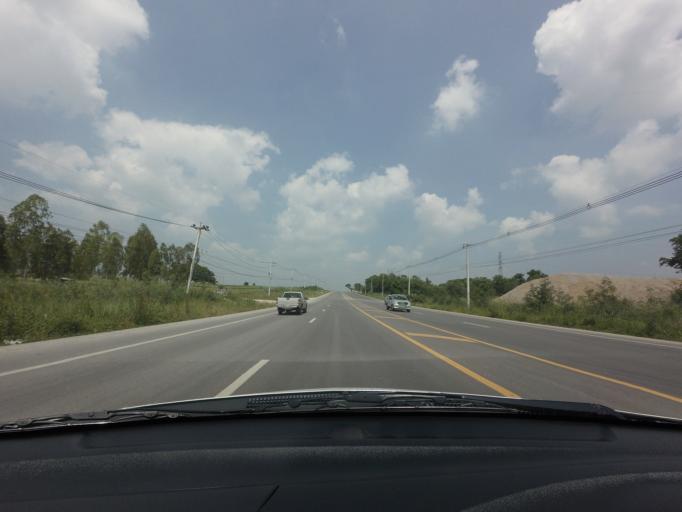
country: TH
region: Nakhon Ratchasima
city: Pak Chong
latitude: 14.6622
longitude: 101.4600
